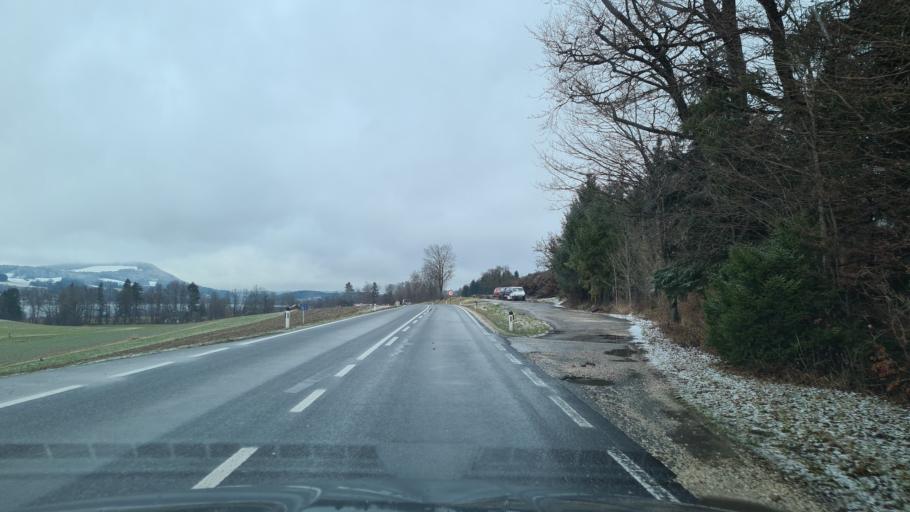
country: AT
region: Upper Austria
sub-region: Politischer Bezirk Vocklabruck
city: Zell am Moos
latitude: 47.9109
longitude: 13.3161
